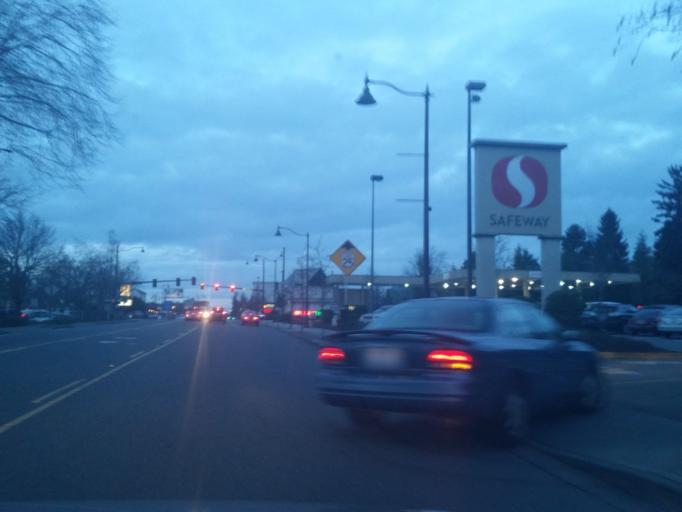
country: US
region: Washington
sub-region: King County
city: Shoreline
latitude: 47.7546
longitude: -122.3134
